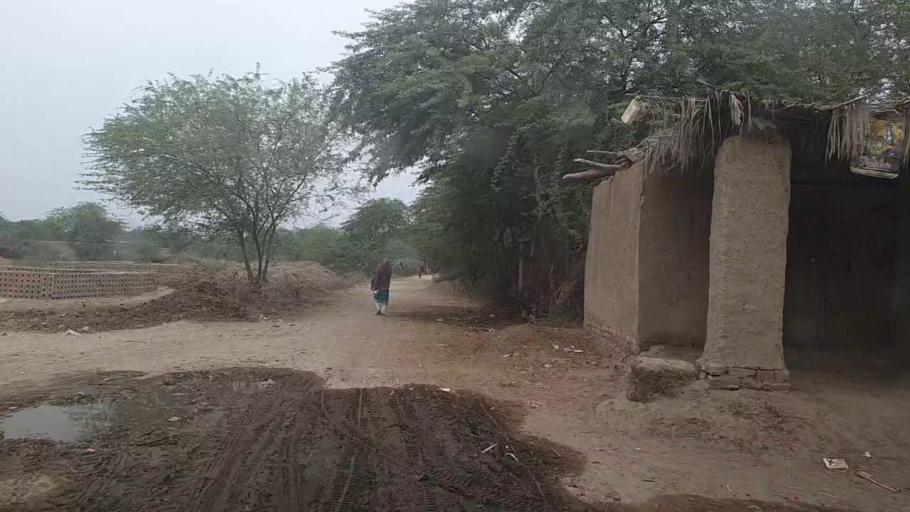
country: PK
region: Sindh
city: Gambat
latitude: 27.3502
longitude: 68.6007
